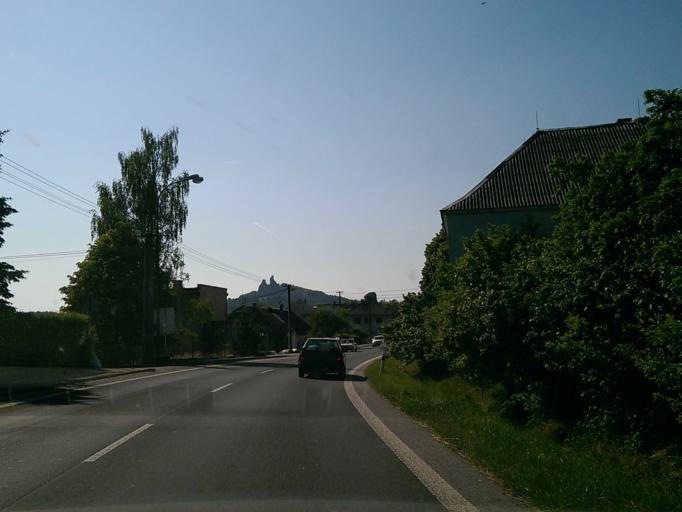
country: CZ
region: Liberecky
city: Rovensko pod Troskami
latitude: 50.5082
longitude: 15.2655
